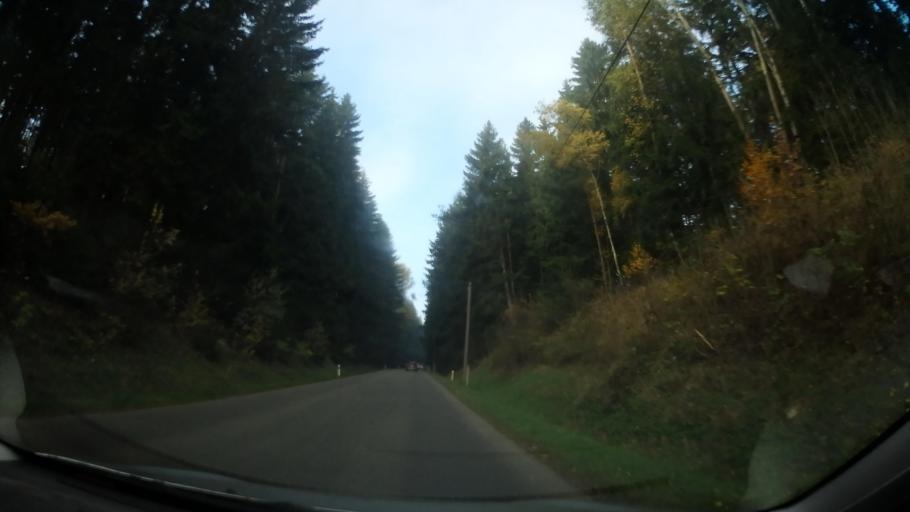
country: CZ
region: Vysocina
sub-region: Okres Zd'ar nad Sazavou
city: Nove Mesto na Morave
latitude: 49.4822
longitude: 16.0179
